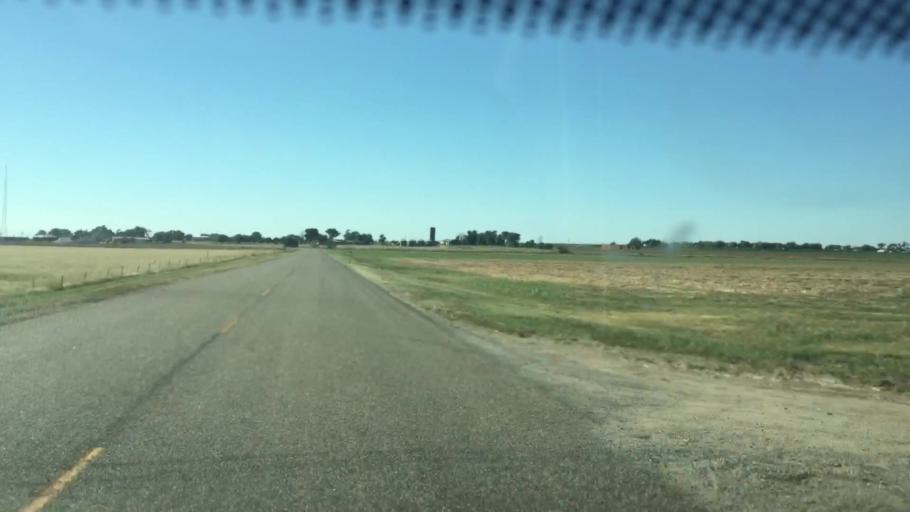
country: US
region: Colorado
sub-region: Prowers County
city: Lamar
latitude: 38.1171
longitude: -102.6043
